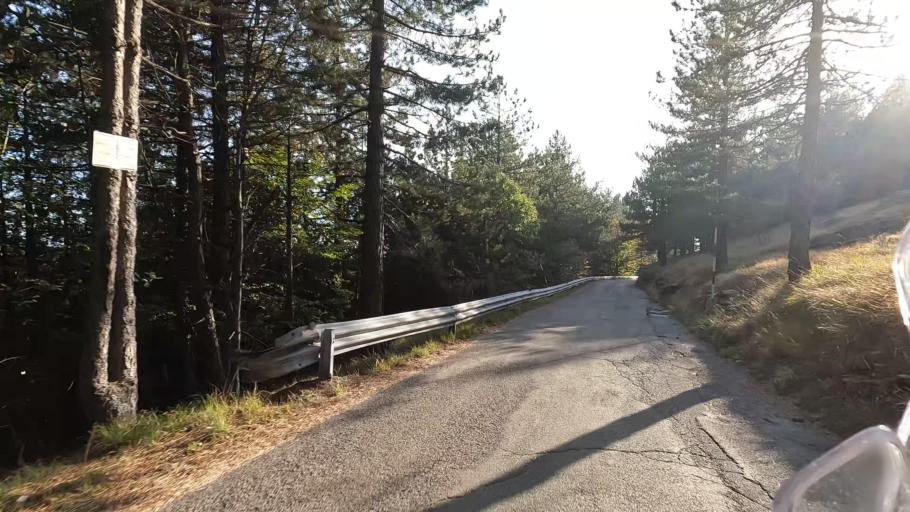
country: IT
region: Liguria
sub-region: Provincia di Savona
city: San Giovanni
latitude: 44.4295
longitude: 8.5430
